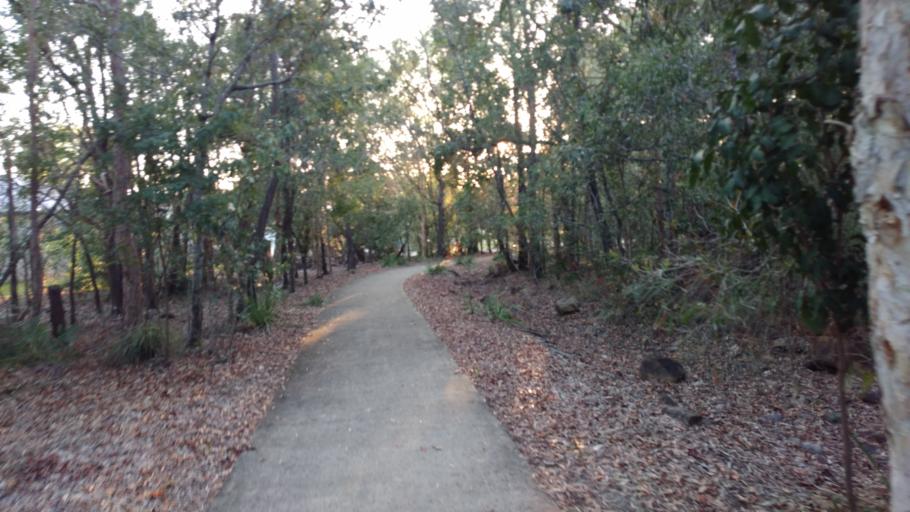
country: AU
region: Queensland
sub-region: Moreton Bay
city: Deception Bay
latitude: -27.2116
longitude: 153.0284
